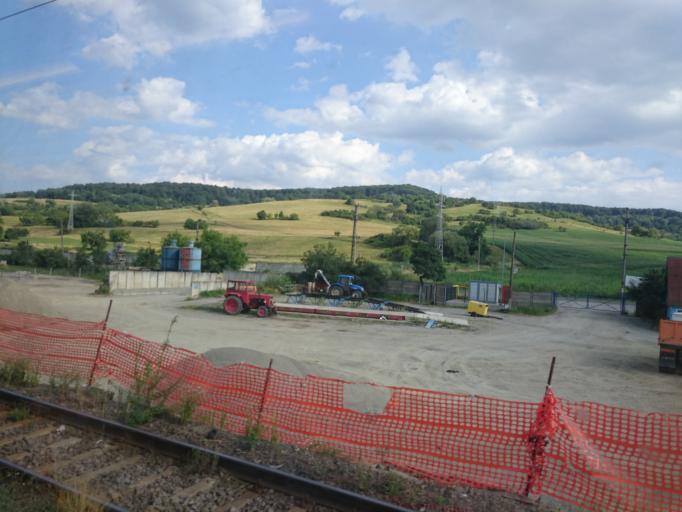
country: RO
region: Sibiu
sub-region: Oras Dumbraveni
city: Dumbraveni
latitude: 46.2158
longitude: 24.5618
